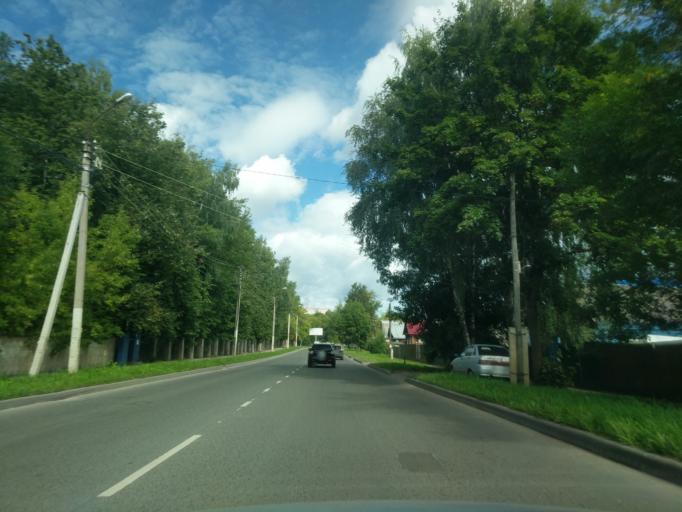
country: RU
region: Kostroma
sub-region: Kostromskoy Rayon
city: Kostroma
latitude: 57.7781
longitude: 40.9564
